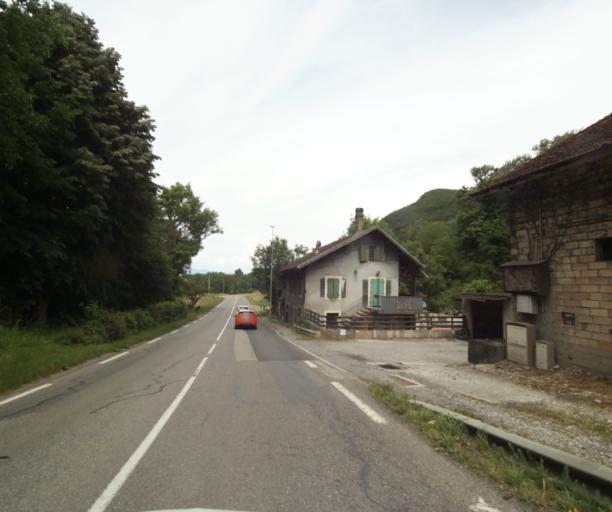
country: FR
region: Rhone-Alpes
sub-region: Departement de la Haute-Savoie
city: Perrignier
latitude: 46.3107
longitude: 6.4407
